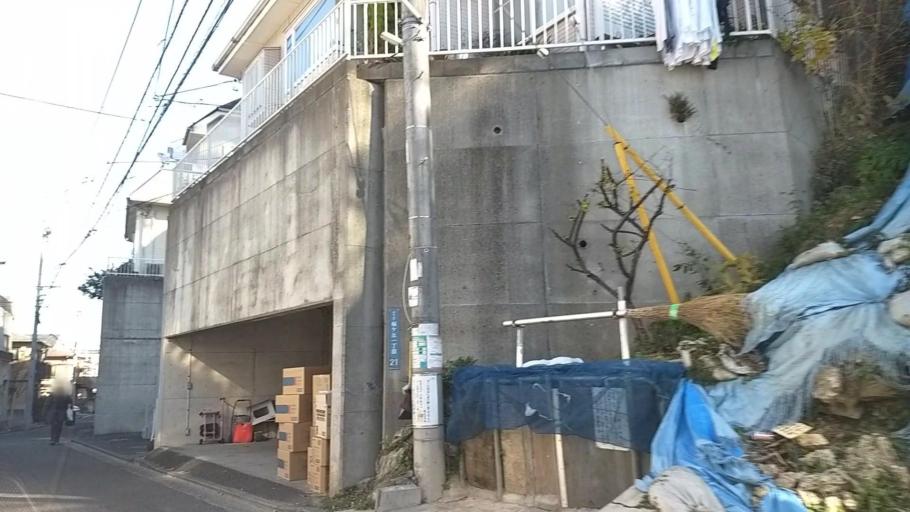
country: JP
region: Kanagawa
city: Yokohama
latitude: 35.4543
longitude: 139.5913
